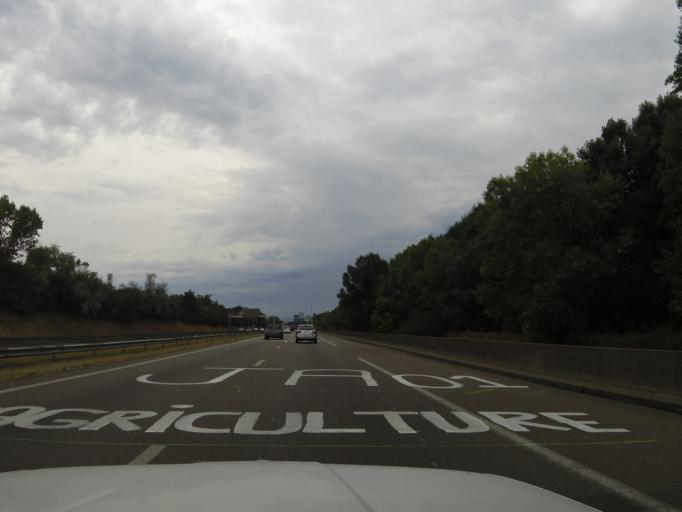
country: FR
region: Rhone-Alpes
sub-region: Departement du Rhone
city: Vaulx-en-Velin
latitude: 45.7922
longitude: 4.9144
